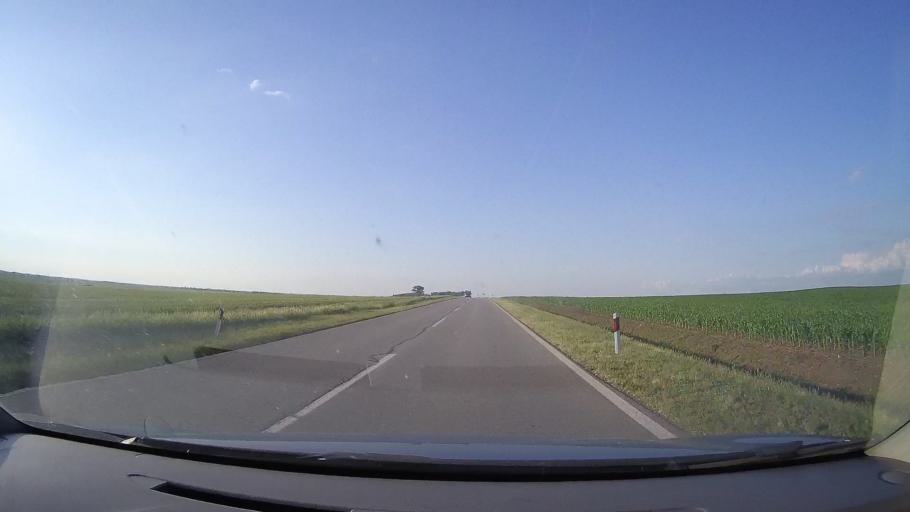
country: RO
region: Timis
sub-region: Comuna Moravita
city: Moravita
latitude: 45.1928
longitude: 21.2991
